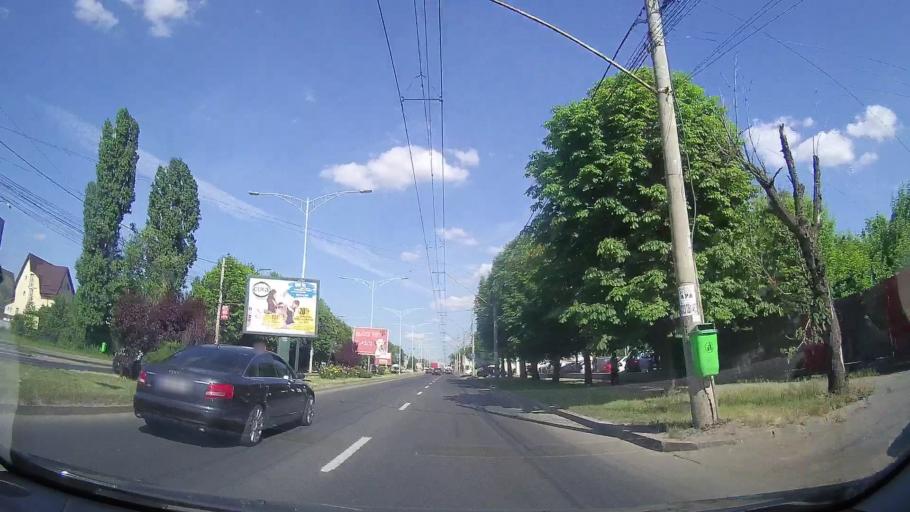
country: RO
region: Ilfov
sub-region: Comuna Chiajna
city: Chiajna
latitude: 44.4348
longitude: 25.9841
